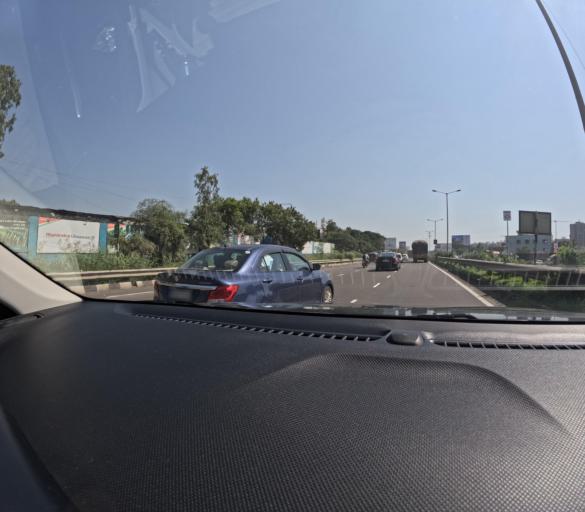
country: IN
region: Maharashtra
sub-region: Pune Division
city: Pimpri
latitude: 18.6290
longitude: 73.7430
